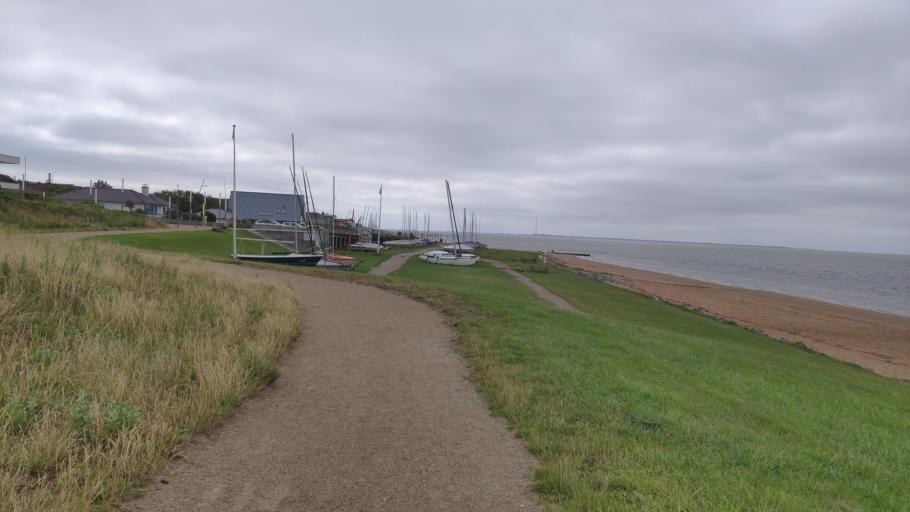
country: DK
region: South Denmark
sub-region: Fano Kommune
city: Nordby
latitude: 55.5282
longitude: 8.3473
